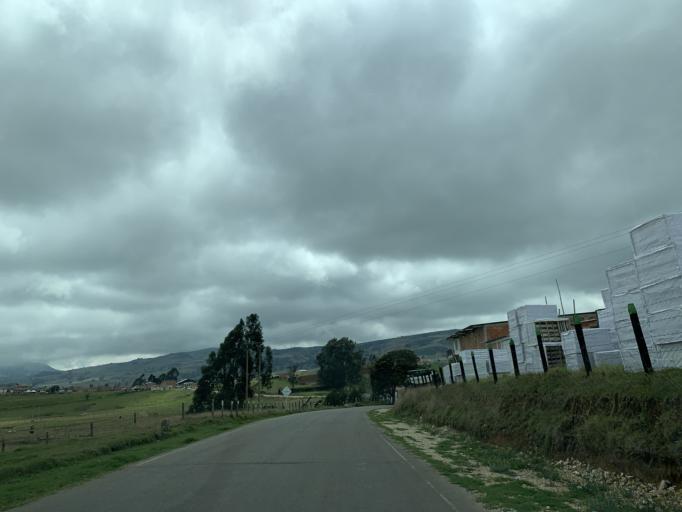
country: CO
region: Boyaca
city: Tunja
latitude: 5.5796
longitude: -73.3616
